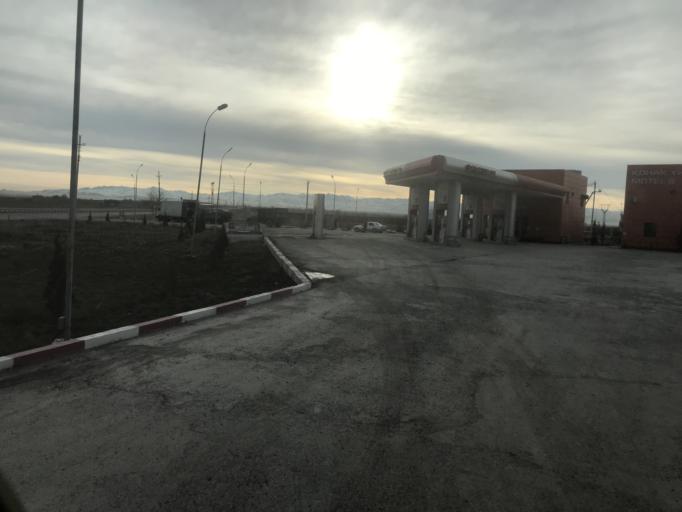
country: KZ
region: Ongtustik Qazaqstan
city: Shymkent
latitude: 42.4625
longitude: 69.5750
